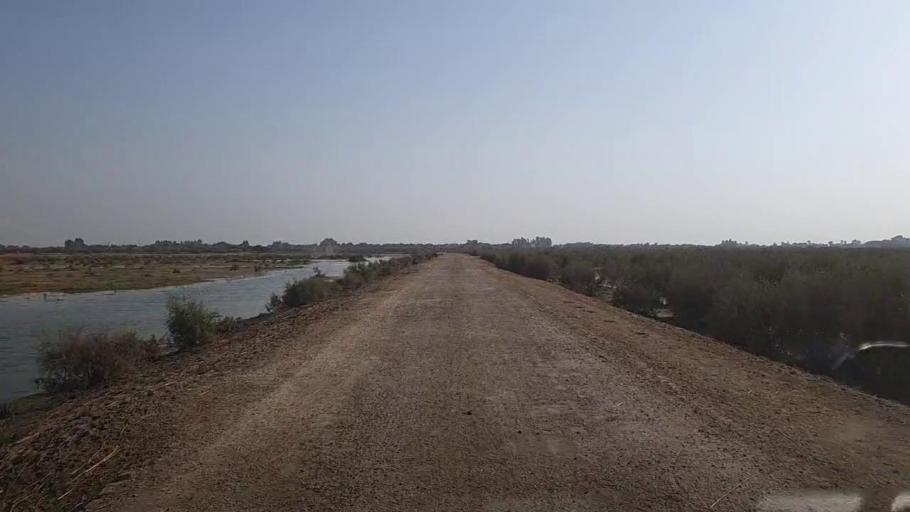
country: PK
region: Sindh
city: Kandhkot
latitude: 28.3622
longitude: 69.3302
